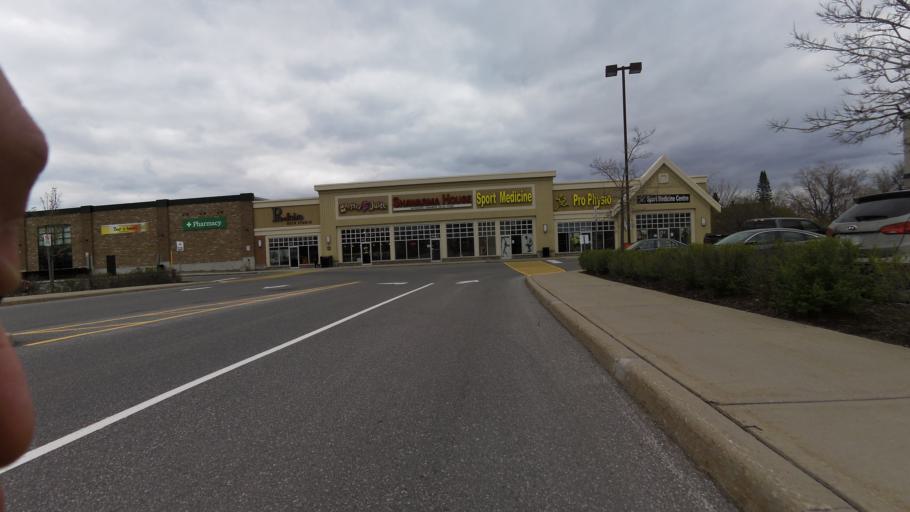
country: CA
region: Ontario
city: Bells Corners
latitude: 45.3570
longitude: -75.9340
